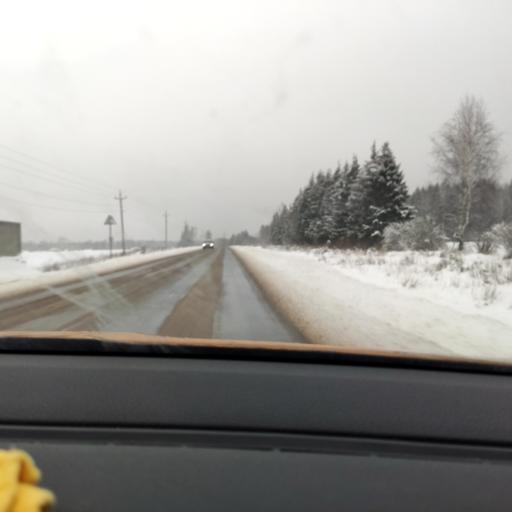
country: RU
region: Moskovskaya
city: Yershovo
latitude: 55.7907
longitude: 36.8497
